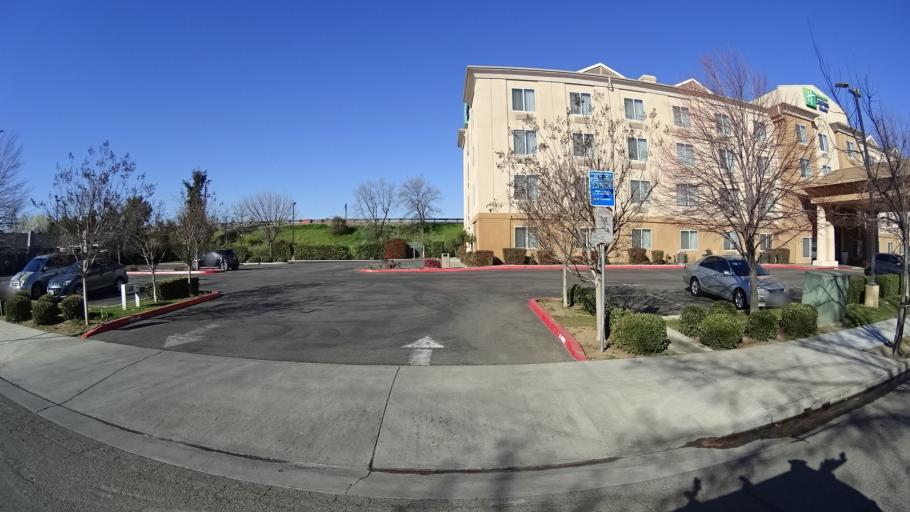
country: US
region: California
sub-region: Fresno County
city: Clovis
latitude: 36.8399
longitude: -119.7839
